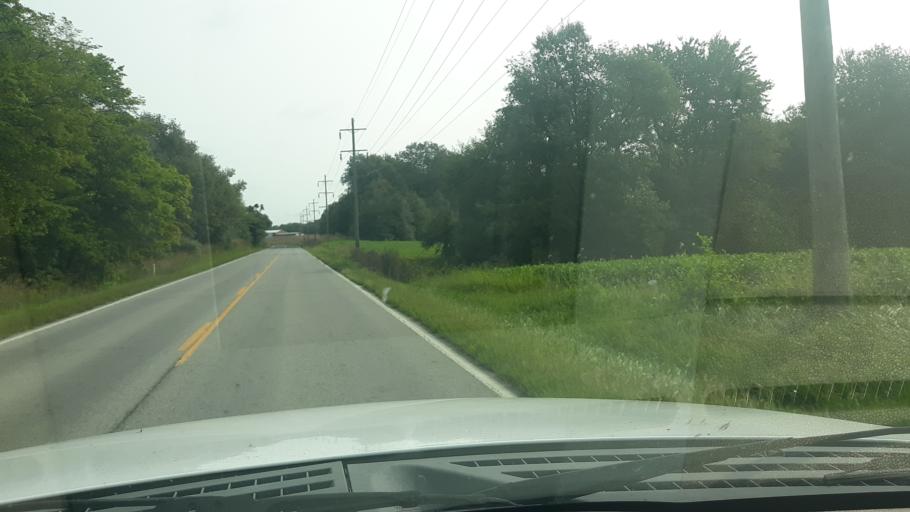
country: US
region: Illinois
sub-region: White County
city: Norris City
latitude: 37.9005
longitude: -88.3647
